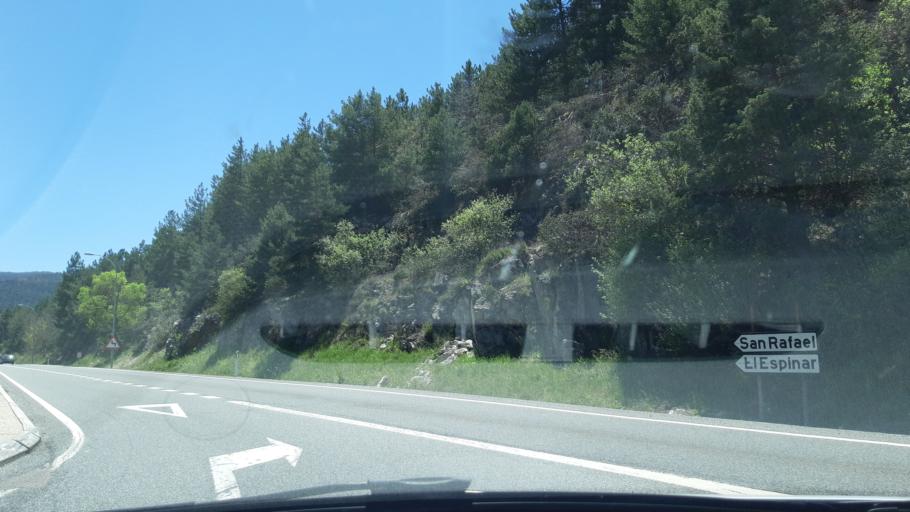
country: ES
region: Castille and Leon
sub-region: Provincia de Segovia
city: Otero de Herreros
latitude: 40.7272
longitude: -4.1969
